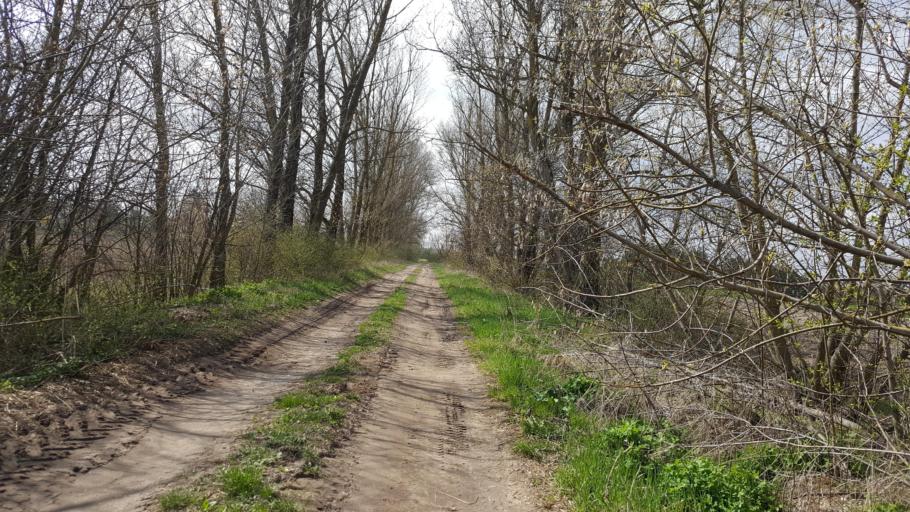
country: BY
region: Brest
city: Kamyanyets
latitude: 52.3352
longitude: 23.9139
